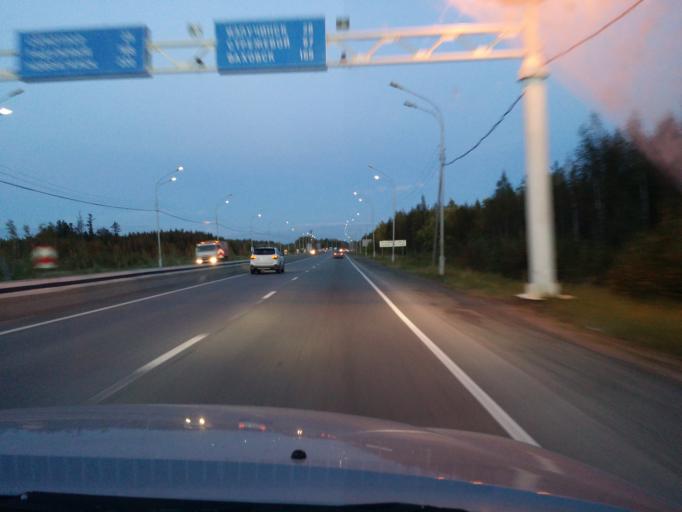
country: RU
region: Khanty-Mansiyskiy Avtonomnyy Okrug
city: Nizhnevartovsk
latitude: 60.9785
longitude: 76.5063
